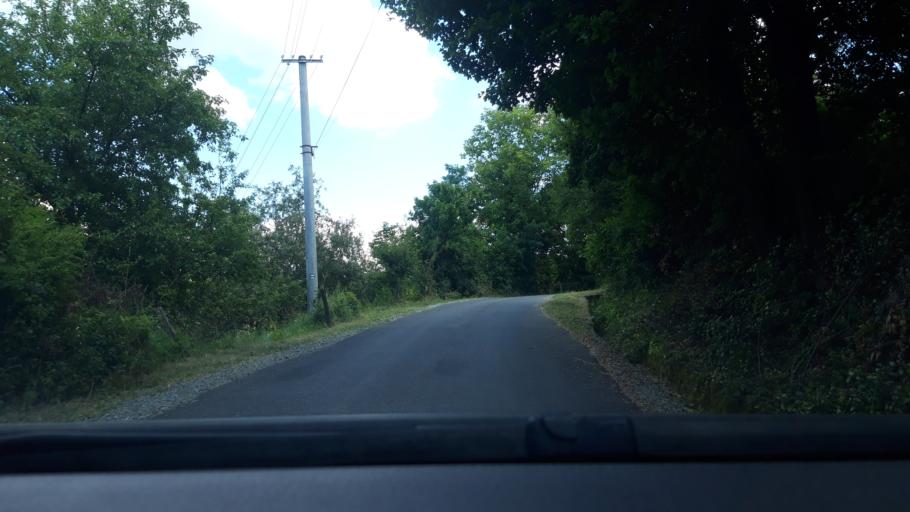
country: HU
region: Nograd
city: Somoskoujfalu
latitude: 48.1849
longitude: 19.8315
